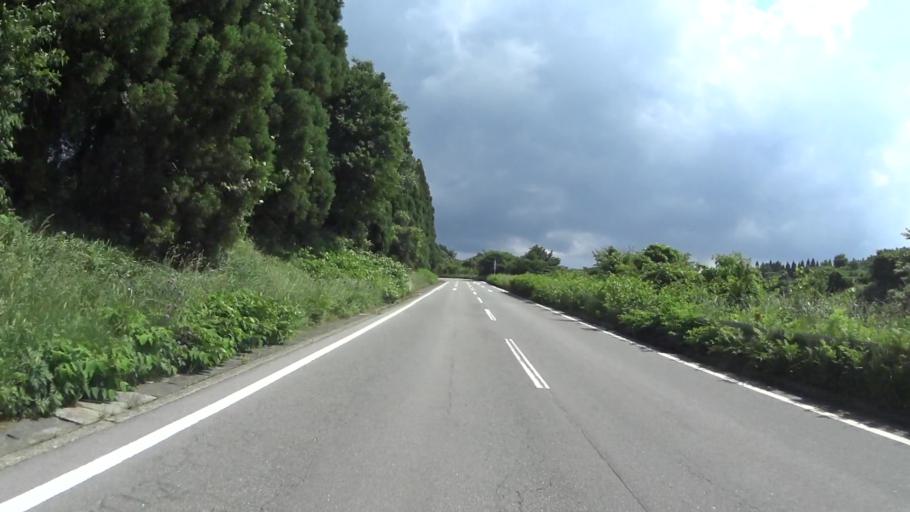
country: JP
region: Kumamoto
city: Aso
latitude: 33.0442
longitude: 131.1665
